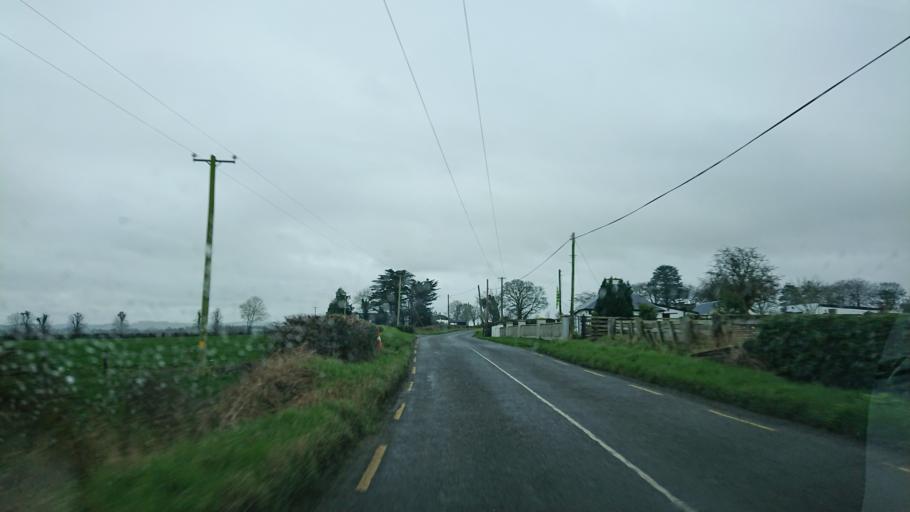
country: IE
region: Leinster
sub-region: Kilkenny
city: Callan
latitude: 52.5269
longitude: -7.2996
